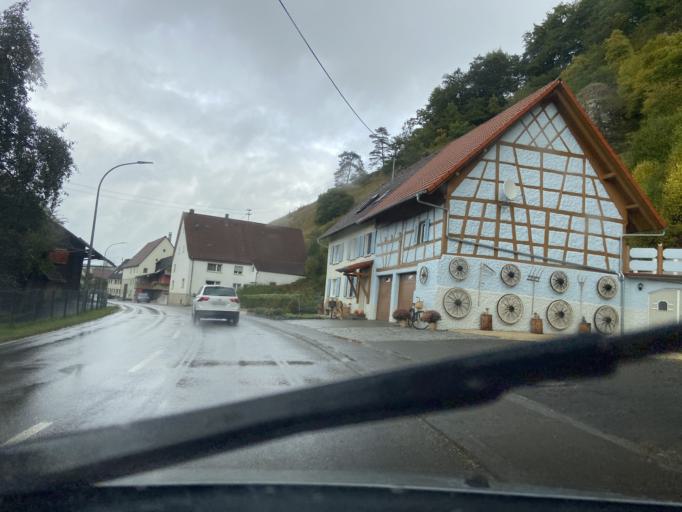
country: DE
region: Baden-Wuerttemberg
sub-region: Tuebingen Region
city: Bingen
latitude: 48.1027
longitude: 9.2894
